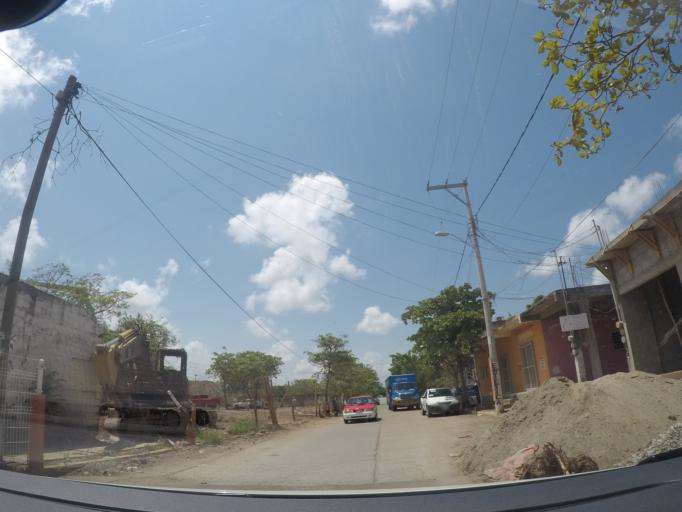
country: MX
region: Oaxaca
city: Juchitan de Zaragoza
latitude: 16.4393
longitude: -95.0180
